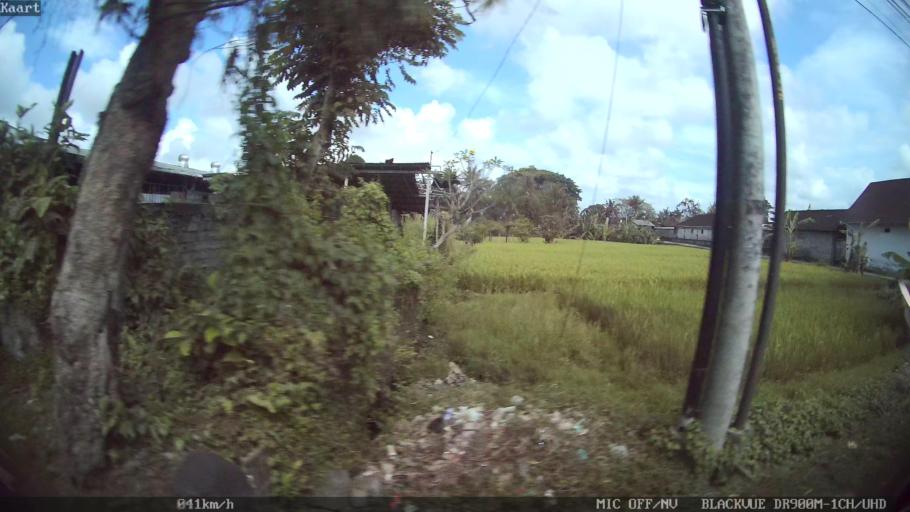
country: ID
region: Bali
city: Banjar Tebongkang
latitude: -8.5500
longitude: 115.2503
